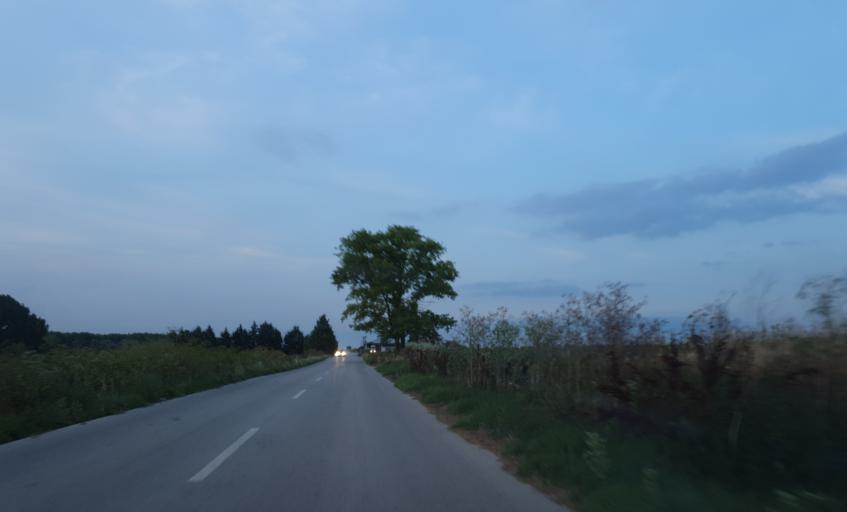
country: TR
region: Tekirdag
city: Beyazkoy
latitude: 41.3927
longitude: 27.6292
